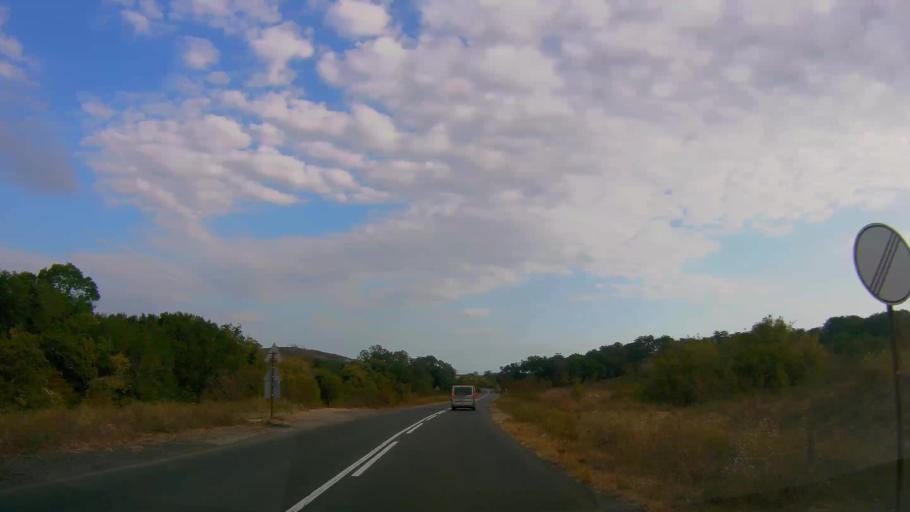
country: BG
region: Burgas
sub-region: Obshtina Primorsko
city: Primorsko
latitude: 42.3231
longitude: 27.7302
